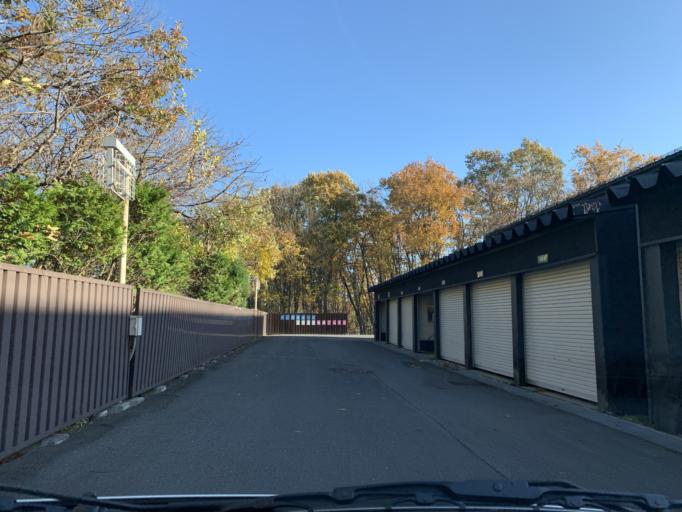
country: JP
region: Iwate
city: Kitakami
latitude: 39.2399
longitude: 141.0952
